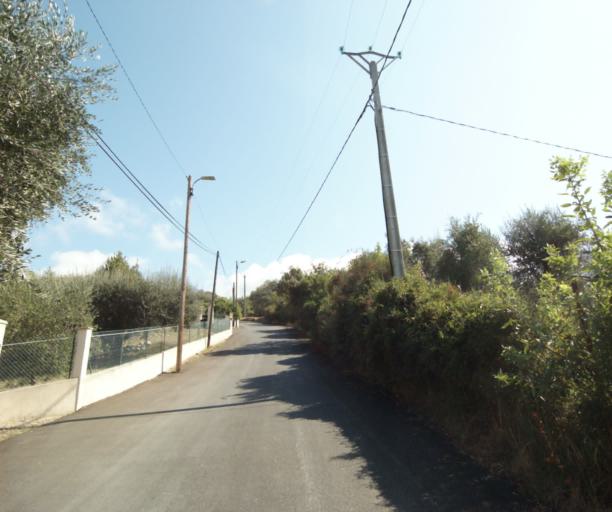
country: FR
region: Provence-Alpes-Cote d'Azur
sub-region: Departement des Alpes-Maritimes
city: Drap
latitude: 43.7568
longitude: 7.3413
